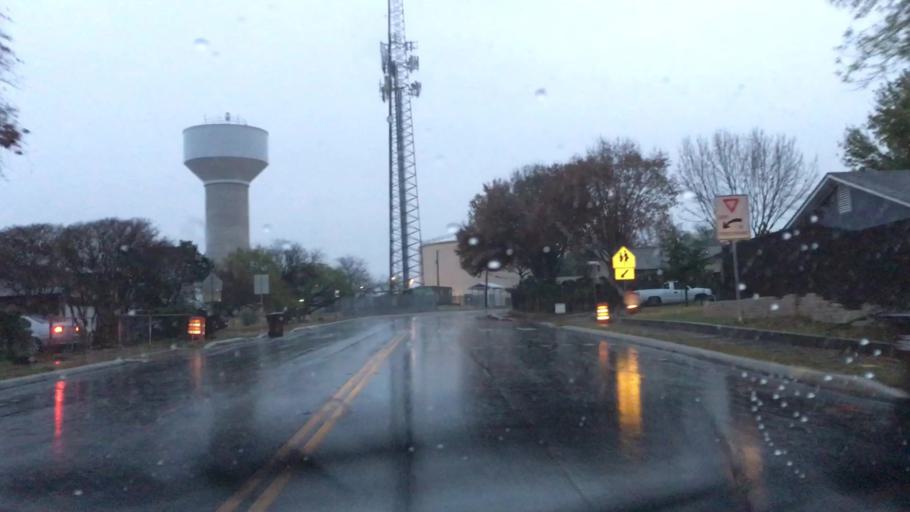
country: US
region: Texas
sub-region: Bexar County
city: Windcrest
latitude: 29.5284
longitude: -98.3534
